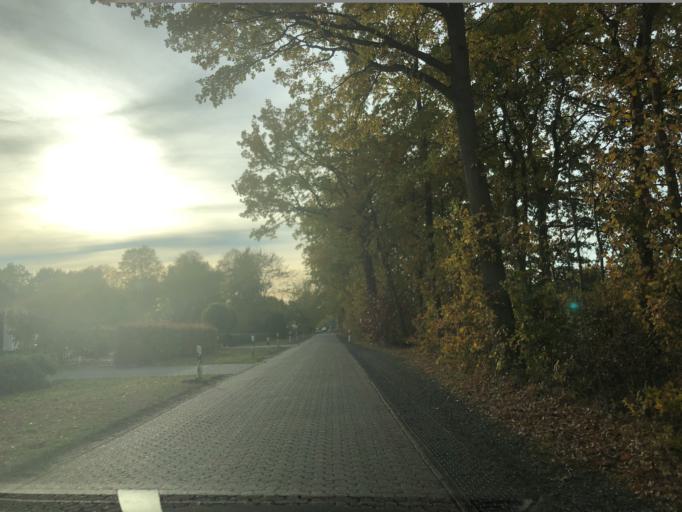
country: DE
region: Lower Saxony
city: Edewecht
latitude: 53.0923
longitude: 8.0789
